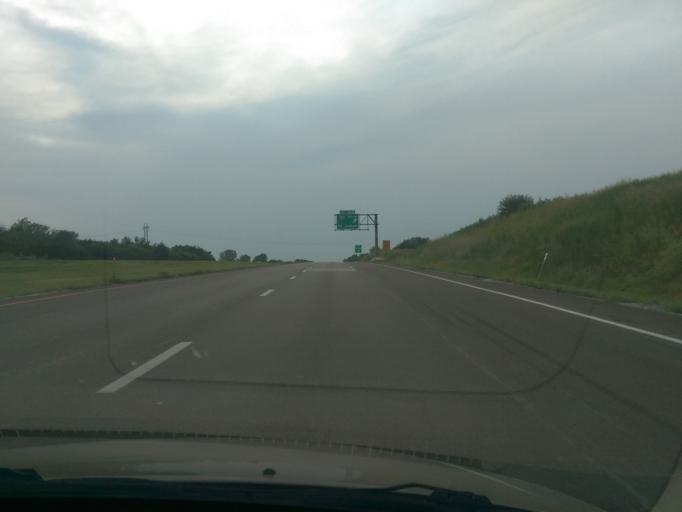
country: US
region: Missouri
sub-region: Andrew County
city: Savannah
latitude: 39.8877
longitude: -94.8584
